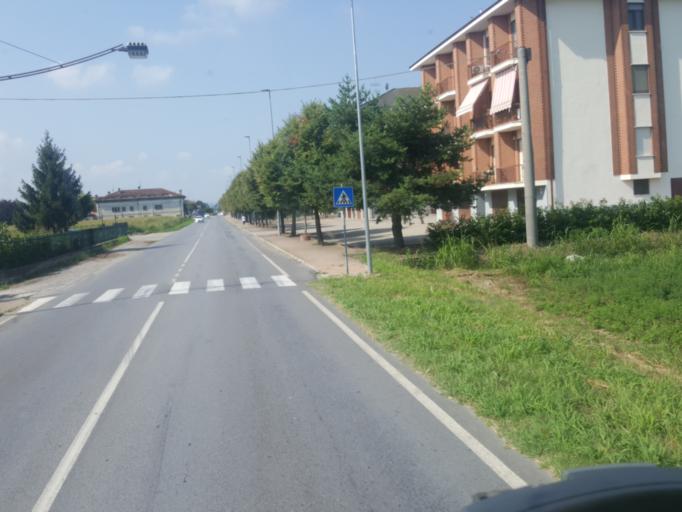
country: IT
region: Piedmont
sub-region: Provincia di Cuneo
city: Vaccheria
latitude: 44.7315
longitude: 8.0470
